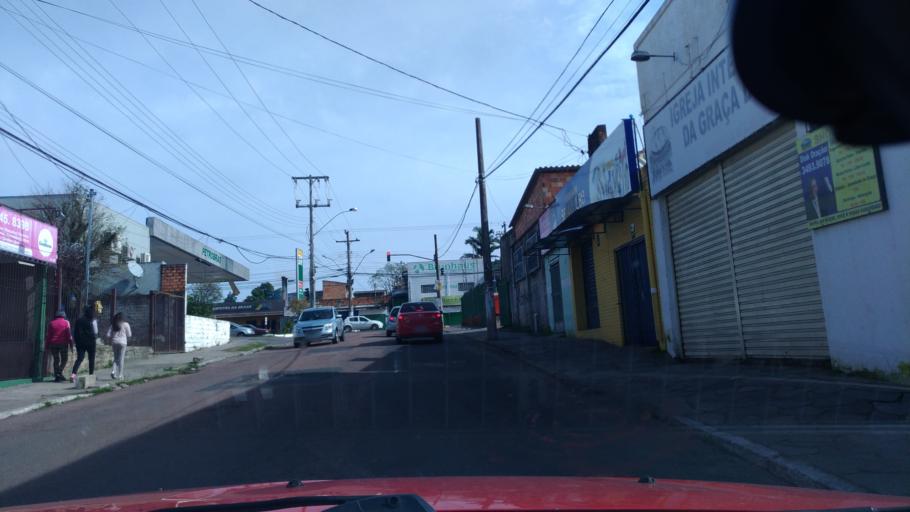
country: BR
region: Rio Grande do Sul
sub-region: Viamao
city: Viamao
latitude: -30.0618
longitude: -51.1075
